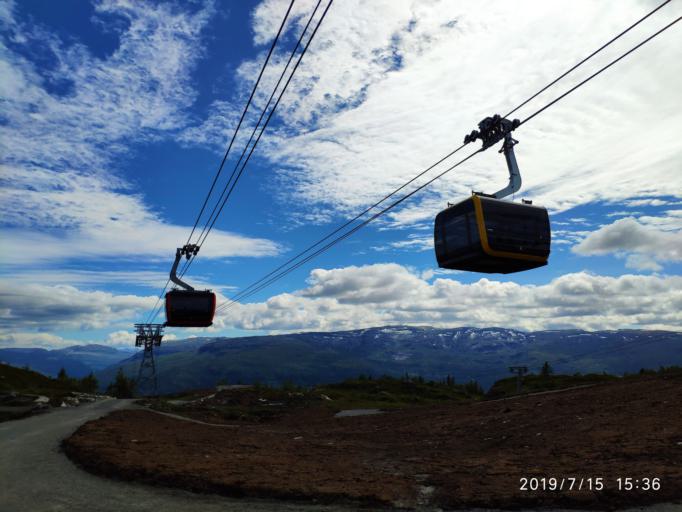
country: NO
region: Hordaland
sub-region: Voss
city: Voss
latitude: 60.6454
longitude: 6.4028
